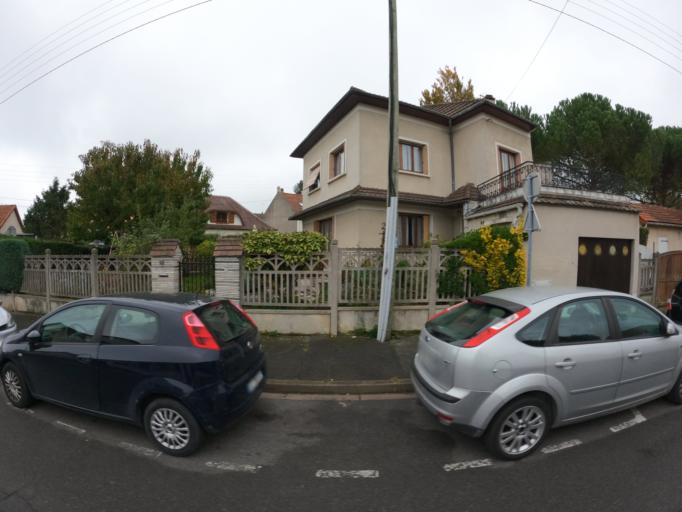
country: FR
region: Ile-de-France
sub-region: Departement du Val-de-Marne
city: Ormesson-sur-Marne
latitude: 48.7883
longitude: 2.5399
